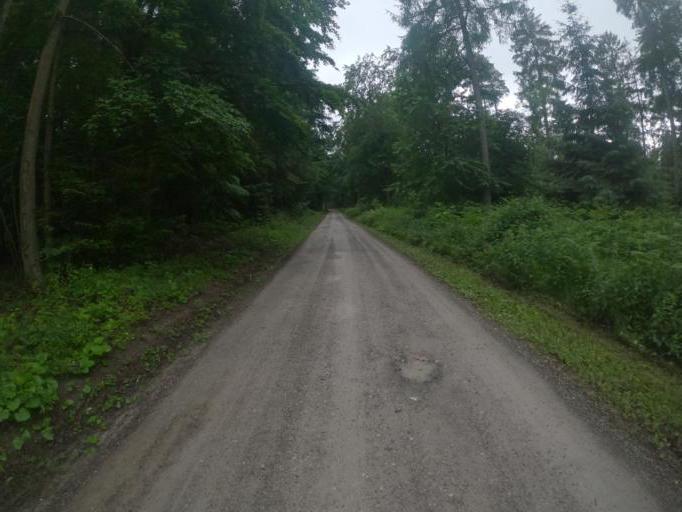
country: DE
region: Baden-Wuerttemberg
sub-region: Regierungsbezirk Stuttgart
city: Schorndorf
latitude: 48.7683
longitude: 9.5383
